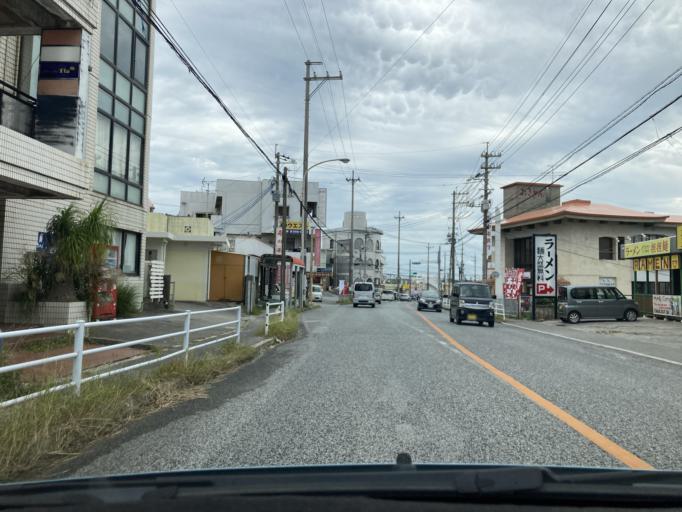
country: JP
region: Okinawa
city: Okinawa
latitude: 26.3824
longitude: 127.7481
